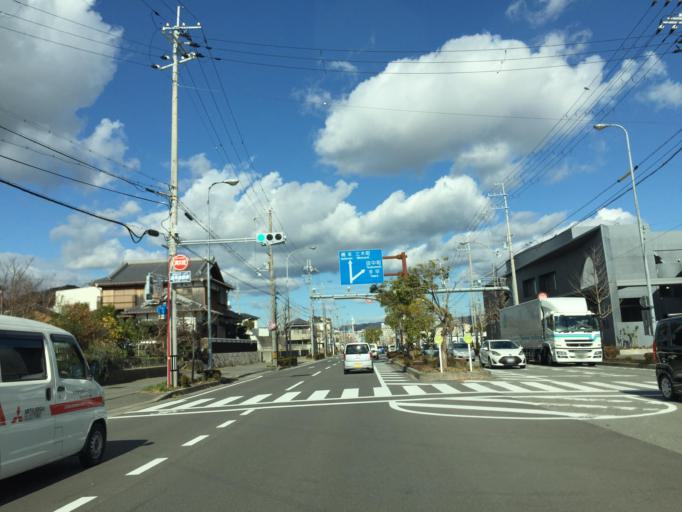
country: JP
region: Wakayama
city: Wakayama-shi
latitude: 34.2169
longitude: 135.1786
